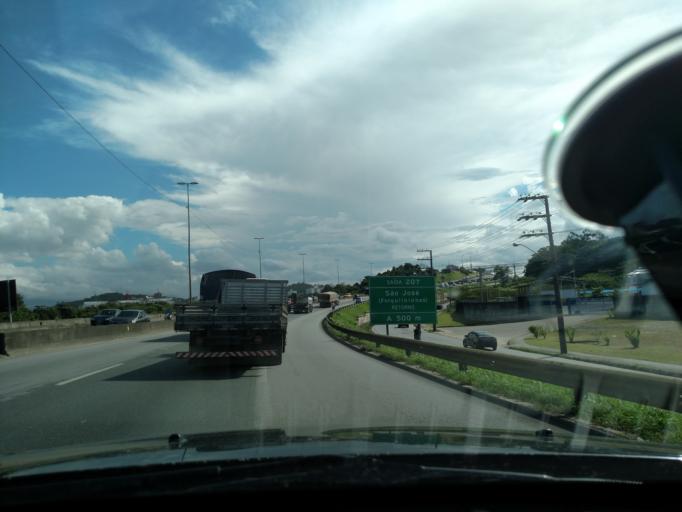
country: BR
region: Santa Catarina
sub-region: Sao Jose
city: Campinas
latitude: -27.6003
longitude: -48.6229
